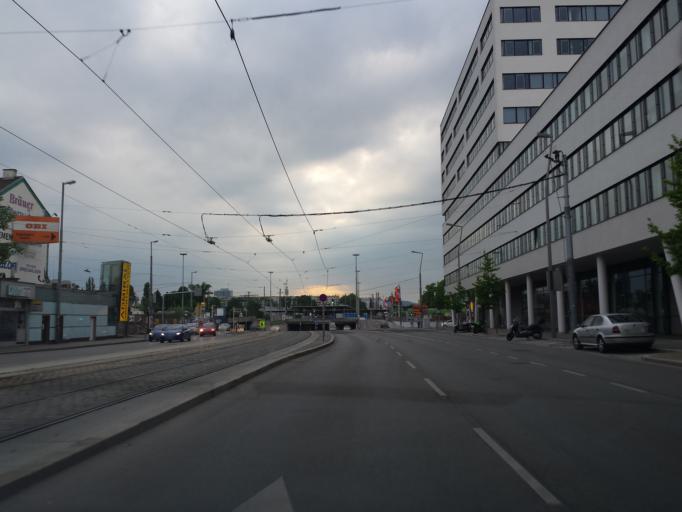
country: AT
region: Lower Austria
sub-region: Politischer Bezirk Wien-Umgebung
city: Gerasdorf bei Wien
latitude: 48.2283
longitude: 16.4571
